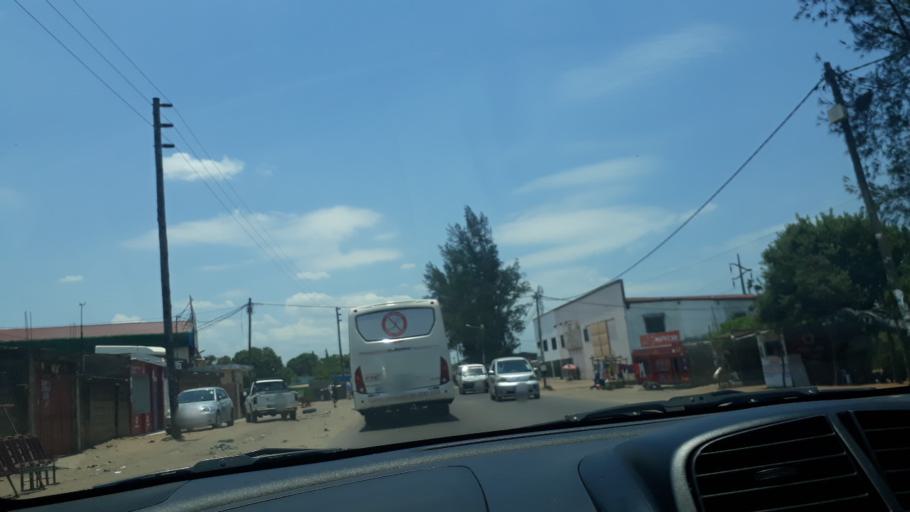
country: MZ
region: Maputo City
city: Maputo
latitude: -25.8939
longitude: 32.6015
